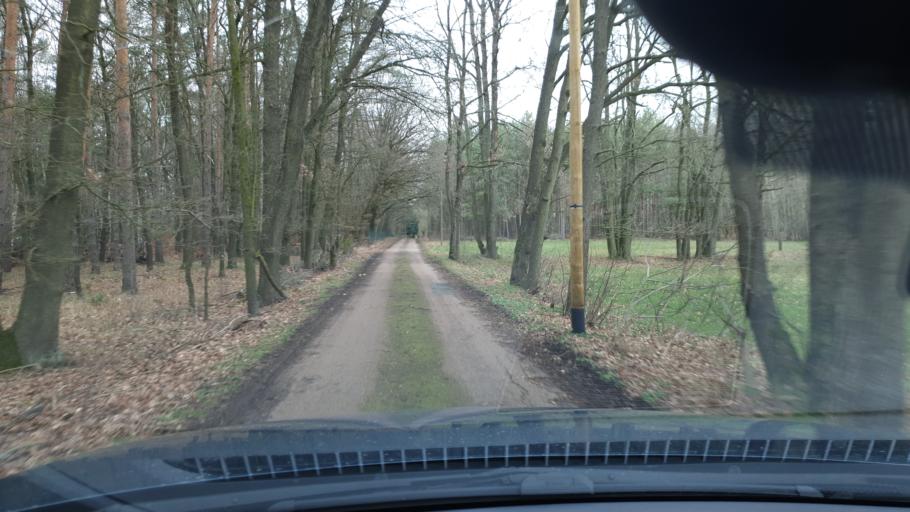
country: DE
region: Saxony-Anhalt
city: Radis
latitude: 51.7484
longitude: 12.5563
